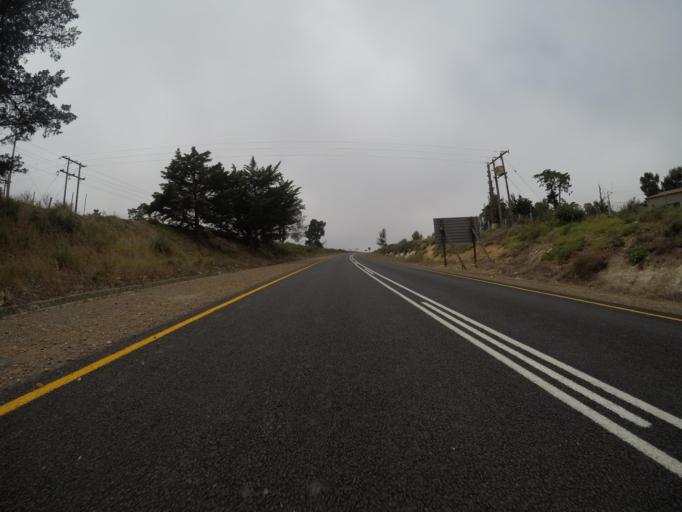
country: ZA
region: Western Cape
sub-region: Eden District Municipality
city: Knysna
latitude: -33.7254
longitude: 23.1674
